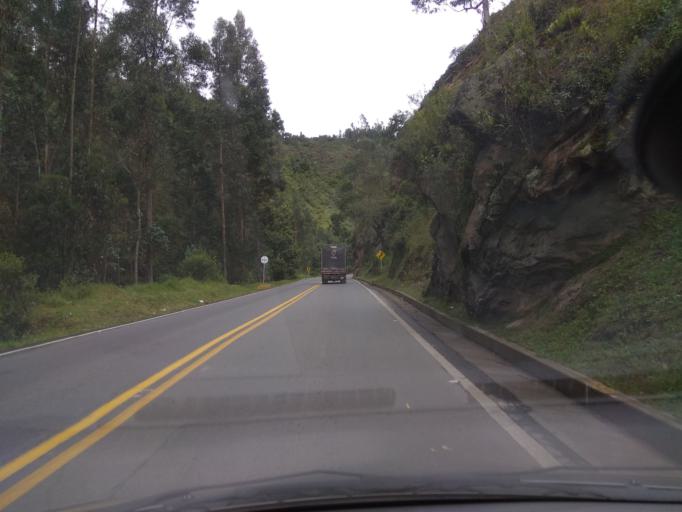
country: CO
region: Boyaca
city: Santa Rosa de Viterbo
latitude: 5.8545
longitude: -73.0119
